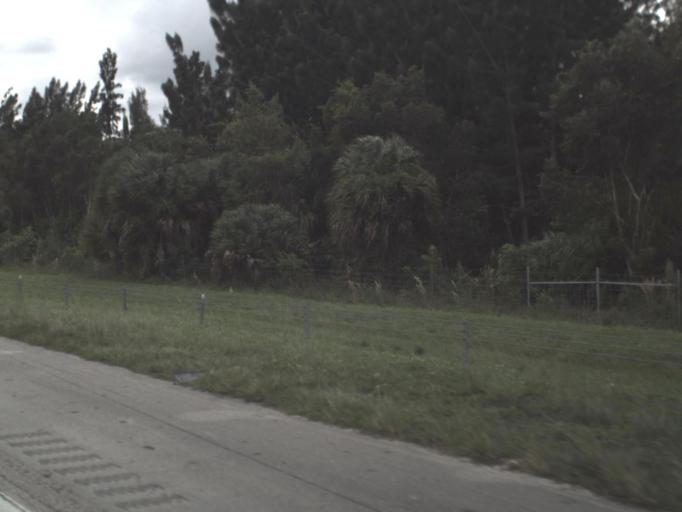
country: US
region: Florida
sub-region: Palm Beach County
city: Schall Circle
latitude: 26.7321
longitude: -80.1353
